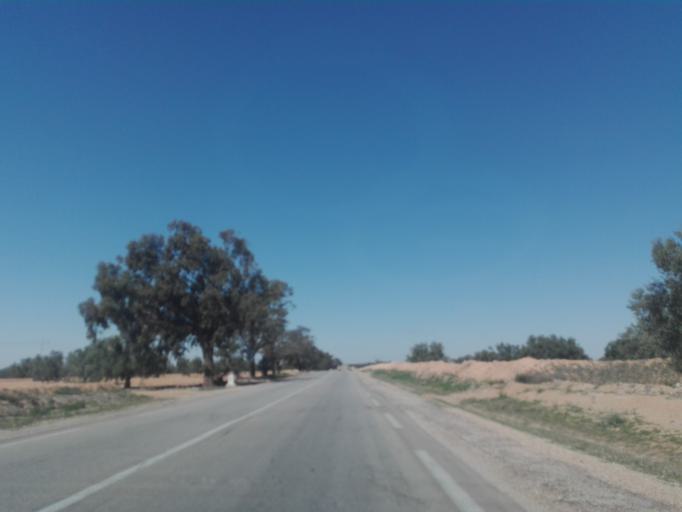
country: TN
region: Safaqis
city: Bi'r `Ali Bin Khalifah
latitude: 34.7568
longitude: 10.3254
